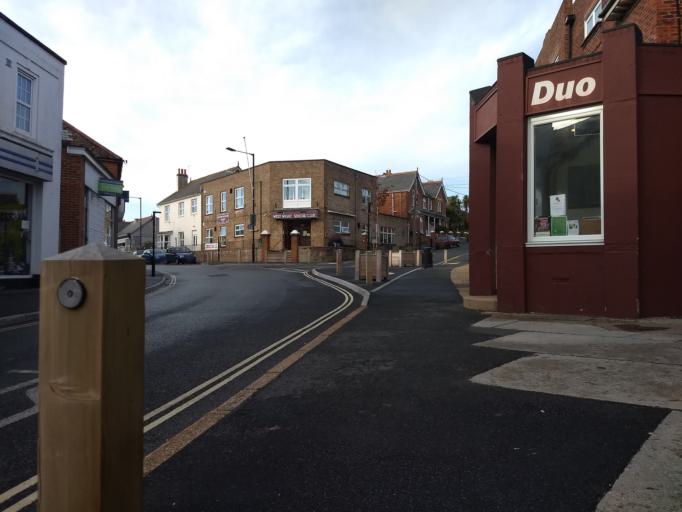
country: GB
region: England
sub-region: Isle of Wight
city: Totland
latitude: 50.6831
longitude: -1.5263
